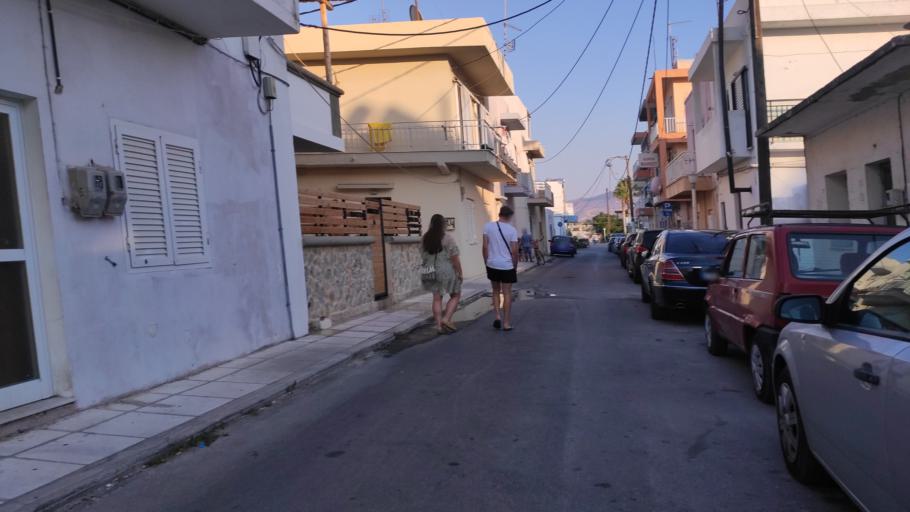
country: GR
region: South Aegean
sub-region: Nomos Dodekanisou
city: Kos
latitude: 36.9010
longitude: 27.2847
